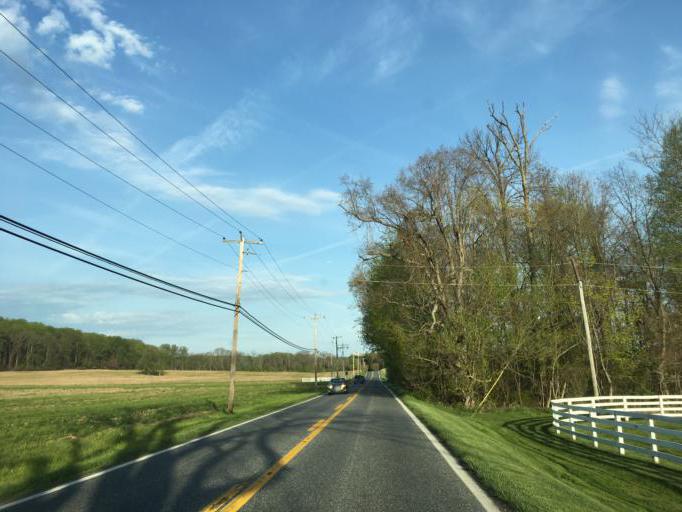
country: US
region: Maryland
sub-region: Baltimore County
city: Reisterstown
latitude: 39.4797
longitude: -76.7763
